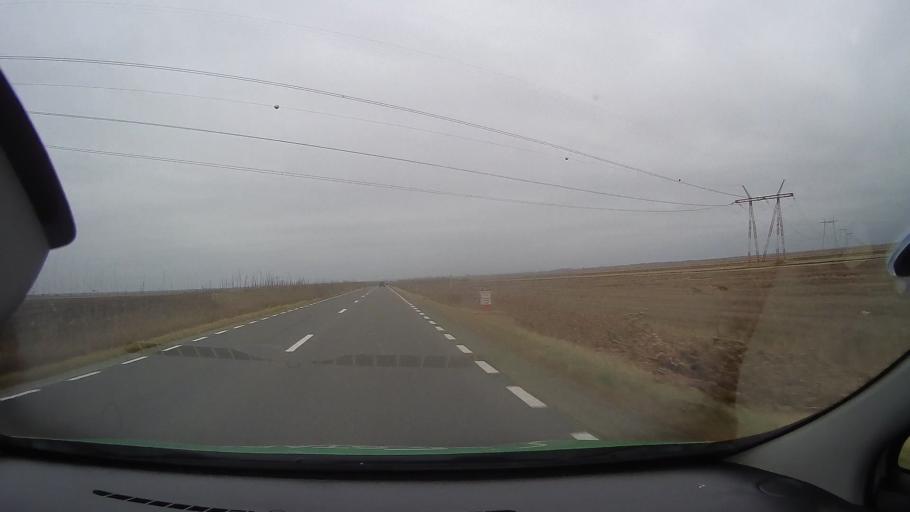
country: RO
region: Ialomita
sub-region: Comuna Gheorghe Lazar
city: Gheorghe Lazar
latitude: 44.6498
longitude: 27.4070
